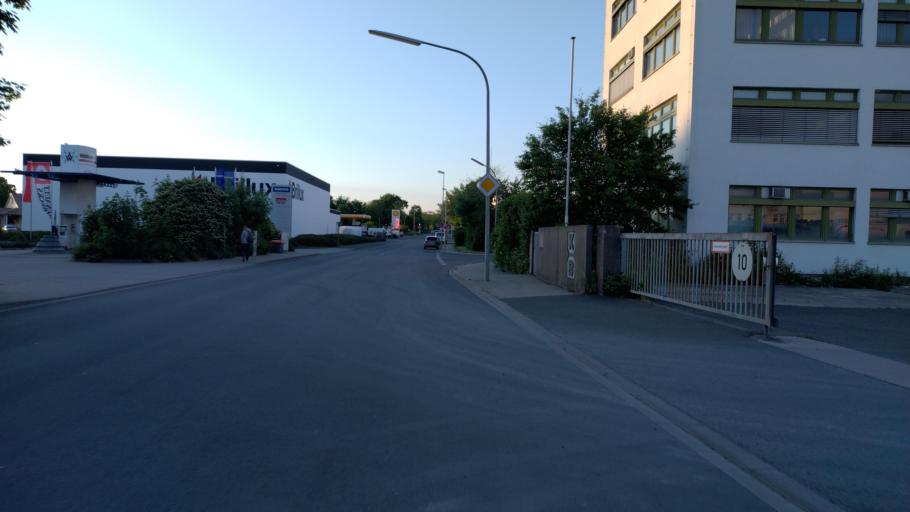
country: DE
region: Bavaria
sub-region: Upper Franconia
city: Bindlach
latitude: 49.9613
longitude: 11.6111
